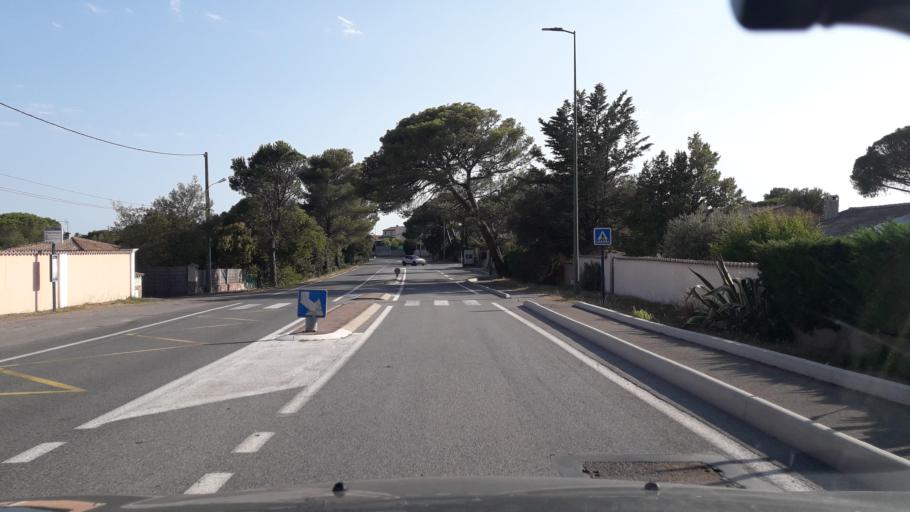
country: FR
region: Provence-Alpes-Cote d'Azur
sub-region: Departement du Var
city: Frejus
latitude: 43.4599
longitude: 6.7577
